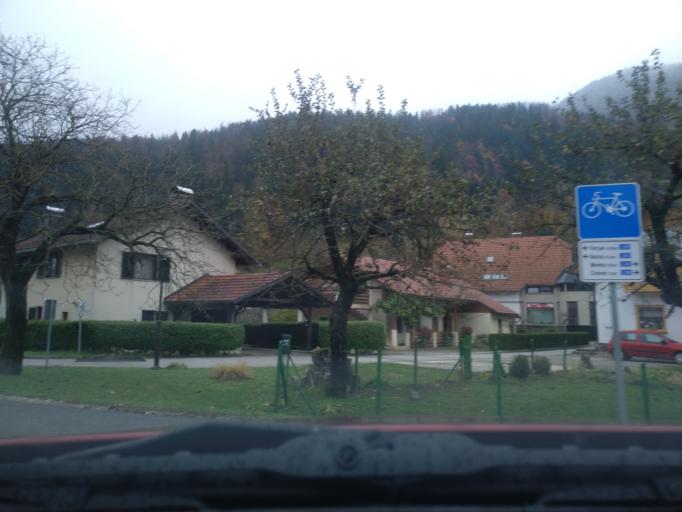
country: SI
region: Gornji Grad
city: Gornji Grad
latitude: 46.2947
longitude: 14.8064
